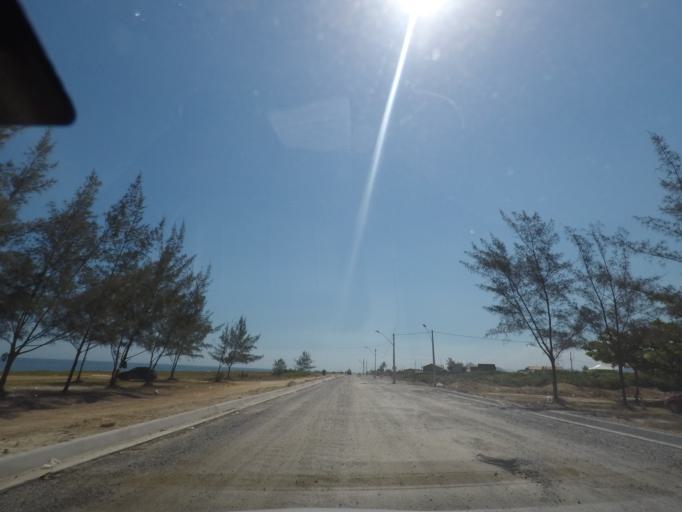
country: BR
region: Rio de Janeiro
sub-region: Marica
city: Marica
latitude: -22.9722
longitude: -42.9068
